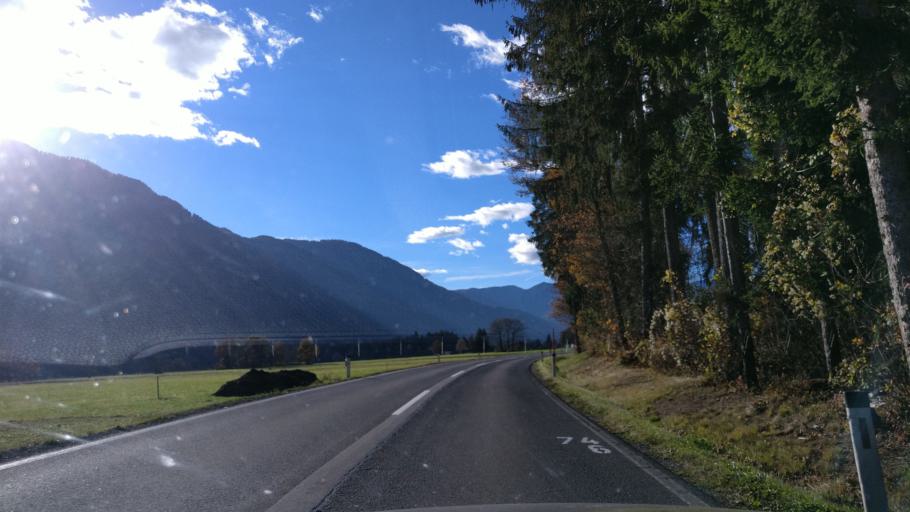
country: AT
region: Carinthia
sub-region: Politischer Bezirk Spittal an der Drau
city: Dellach im Drautal
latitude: 46.7384
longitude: 13.0974
